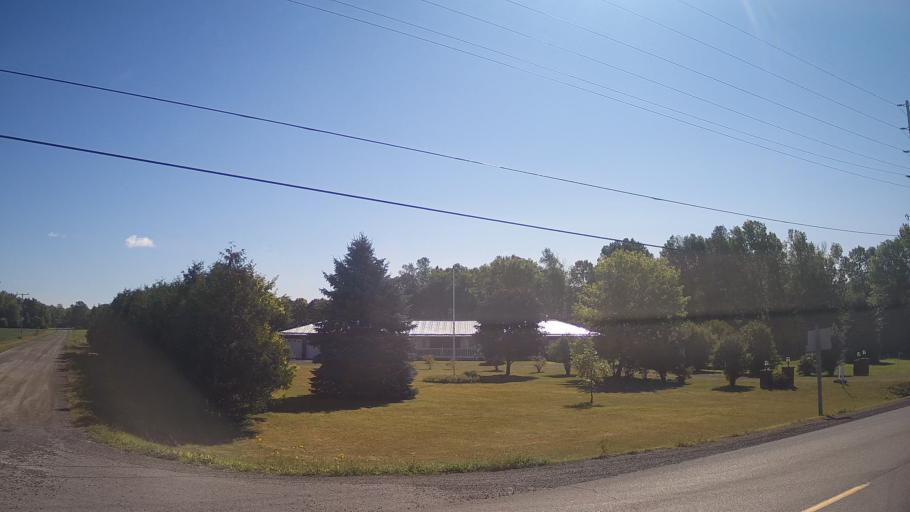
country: CA
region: Ontario
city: Prescott
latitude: 44.9811
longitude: -75.5414
